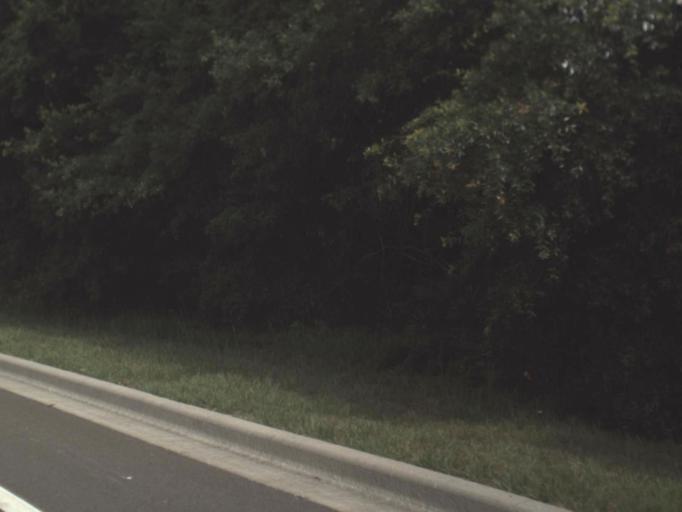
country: US
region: Florida
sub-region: Duval County
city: Jacksonville
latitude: 30.4157
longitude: -81.5931
